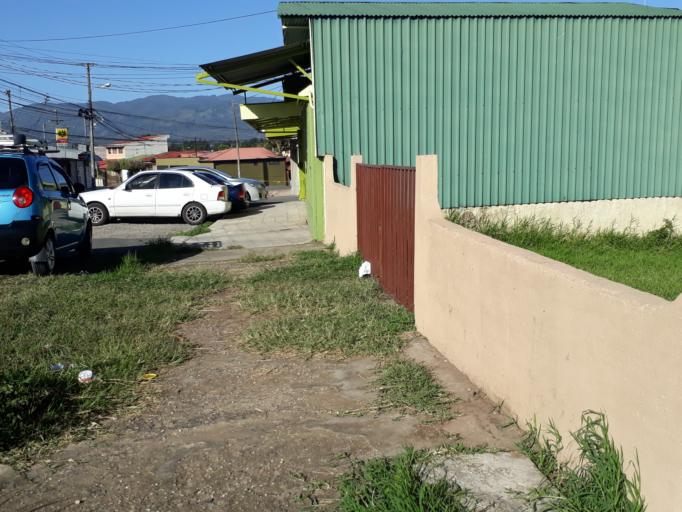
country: CR
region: Cartago
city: Cartago
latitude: 9.8741
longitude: -83.9414
